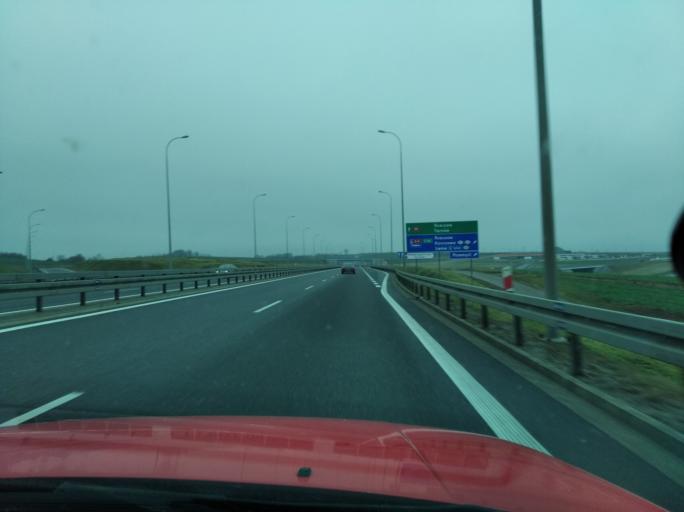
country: PL
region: Subcarpathian Voivodeship
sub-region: Powiat jaroslawski
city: Wierzbna
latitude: 50.0359
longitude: 22.5825
